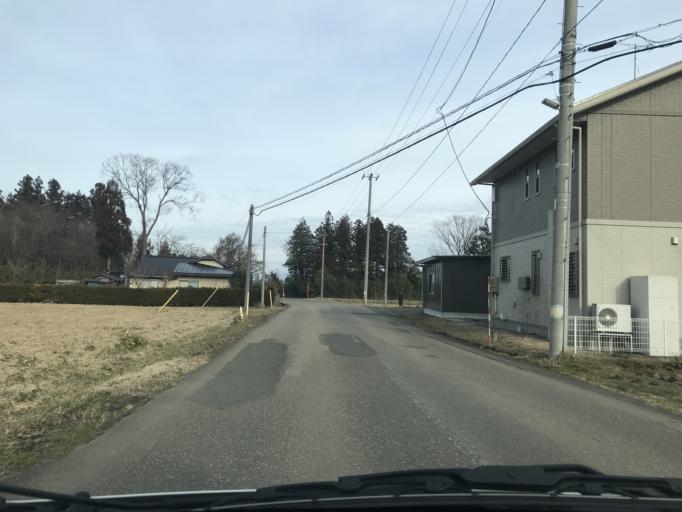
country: JP
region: Iwate
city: Mizusawa
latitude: 39.1716
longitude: 141.0577
